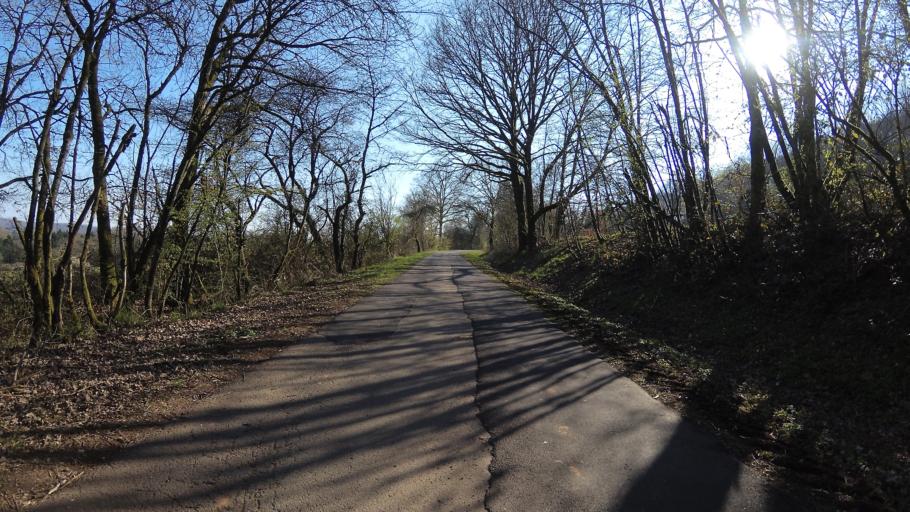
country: DE
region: Saarland
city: Ottweiler
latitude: 49.3895
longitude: 7.1668
